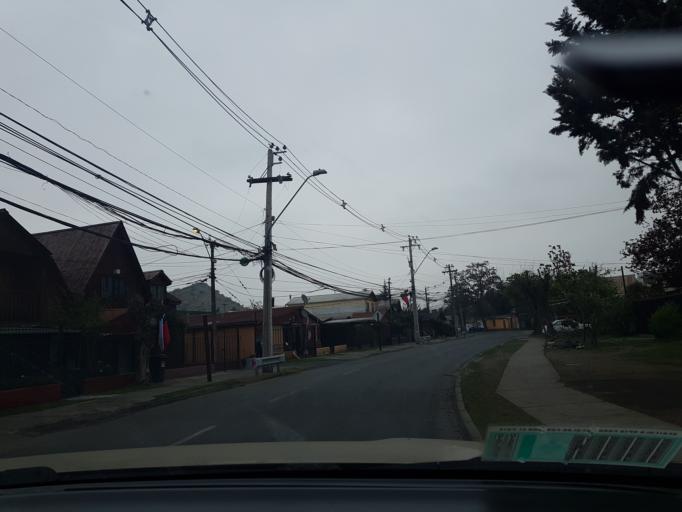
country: CL
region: Santiago Metropolitan
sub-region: Provincia de Santiago
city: Lo Prado
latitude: -33.3700
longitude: -70.7305
